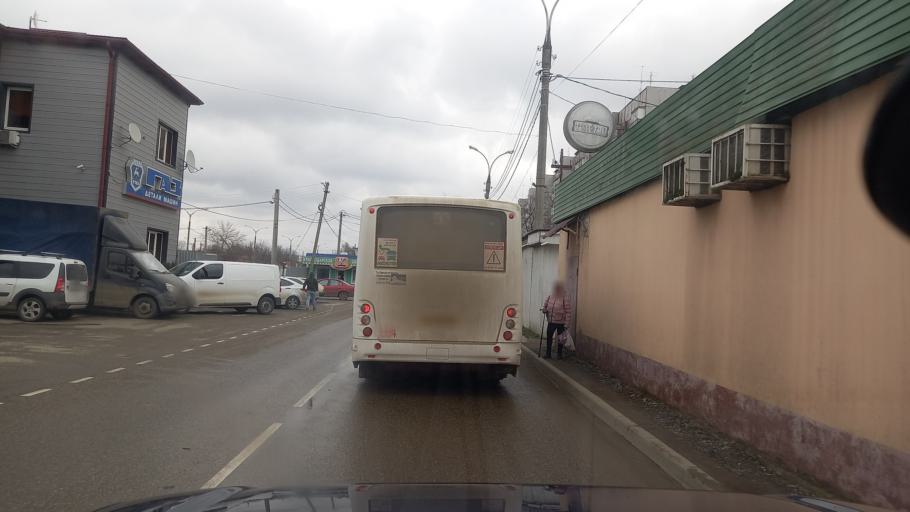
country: RU
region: Krasnodarskiy
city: Pashkovskiy
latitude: 45.0429
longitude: 39.1098
